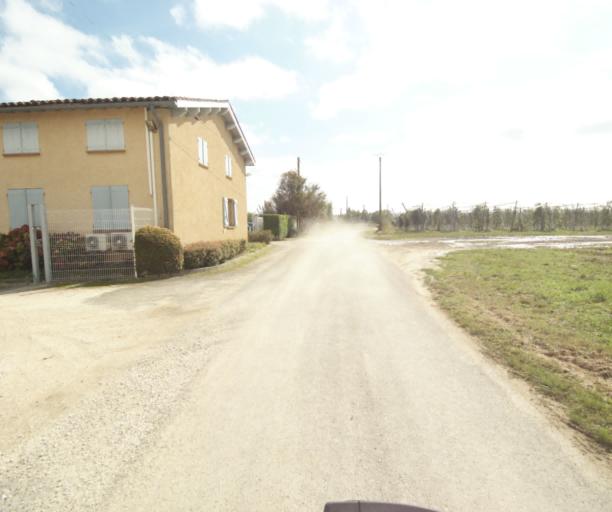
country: FR
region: Midi-Pyrenees
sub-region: Departement du Tarn-et-Garonne
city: Montech
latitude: 43.9424
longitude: 1.2063
